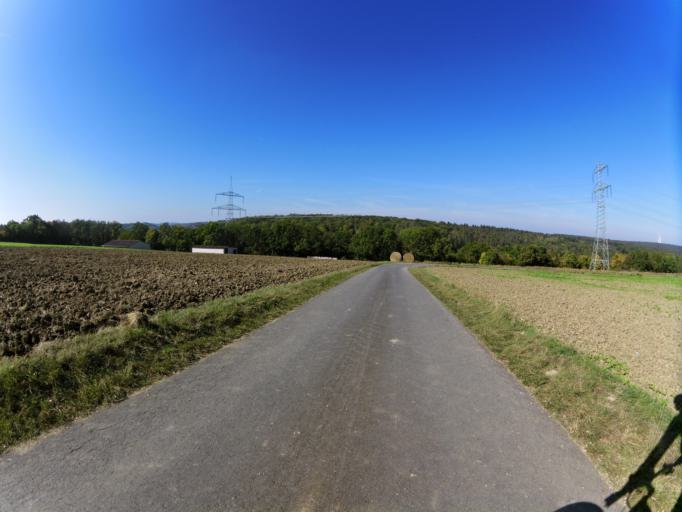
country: DE
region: Bavaria
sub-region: Regierungsbezirk Unterfranken
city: Ochsenfurt
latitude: 49.6793
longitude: 10.0525
